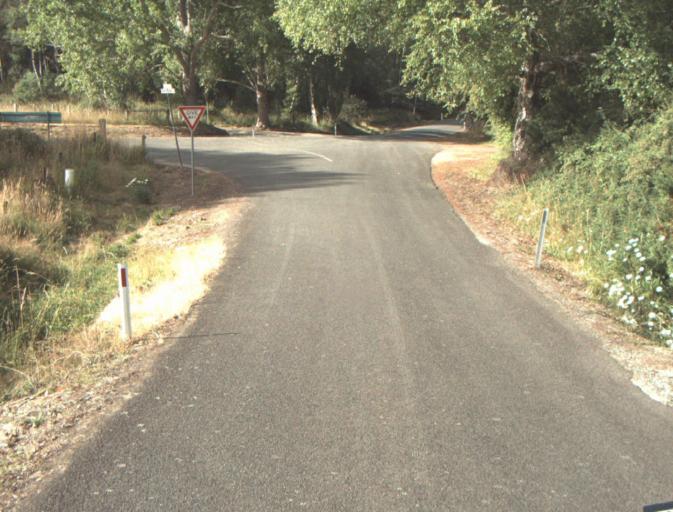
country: AU
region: Tasmania
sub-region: Launceston
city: Mayfield
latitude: -41.2902
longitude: 147.2060
